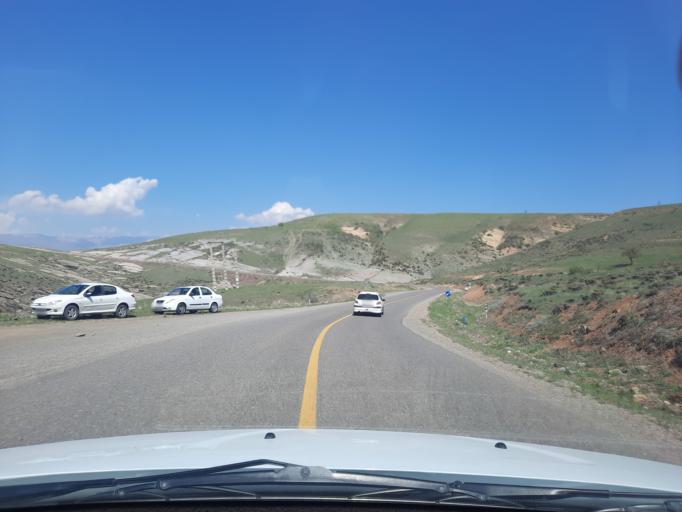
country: IR
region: Qazvin
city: Qazvin
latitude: 36.4080
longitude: 50.2329
